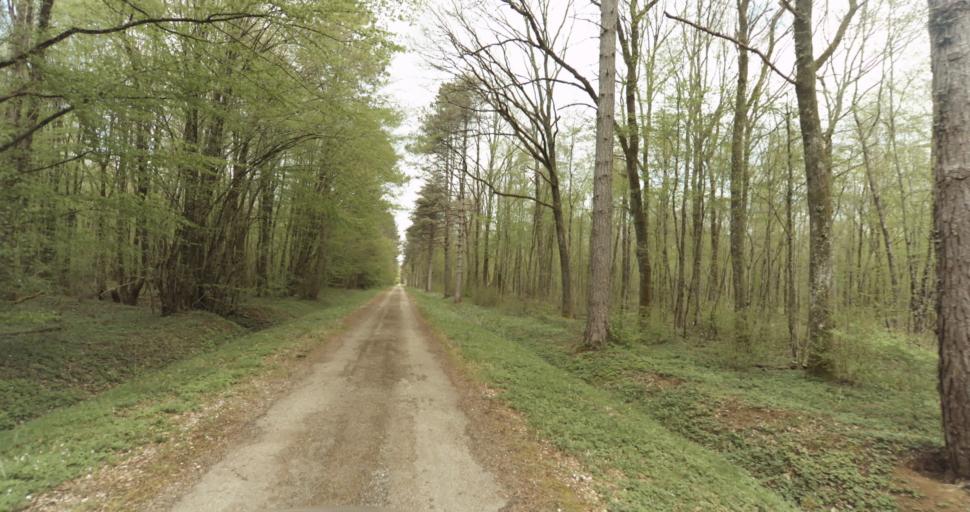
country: FR
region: Bourgogne
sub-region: Departement de la Cote-d'Or
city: Auxonne
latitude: 47.1553
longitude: 5.4223
